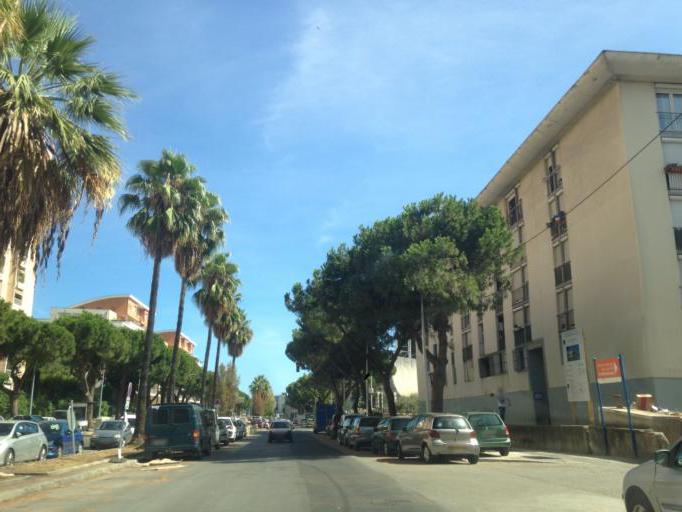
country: FR
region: Provence-Alpes-Cote d'Azur
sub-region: Departement des Alpes-Maritimes
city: Saint-Laurent-du-Var
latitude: 43.6744
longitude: 7.2077
